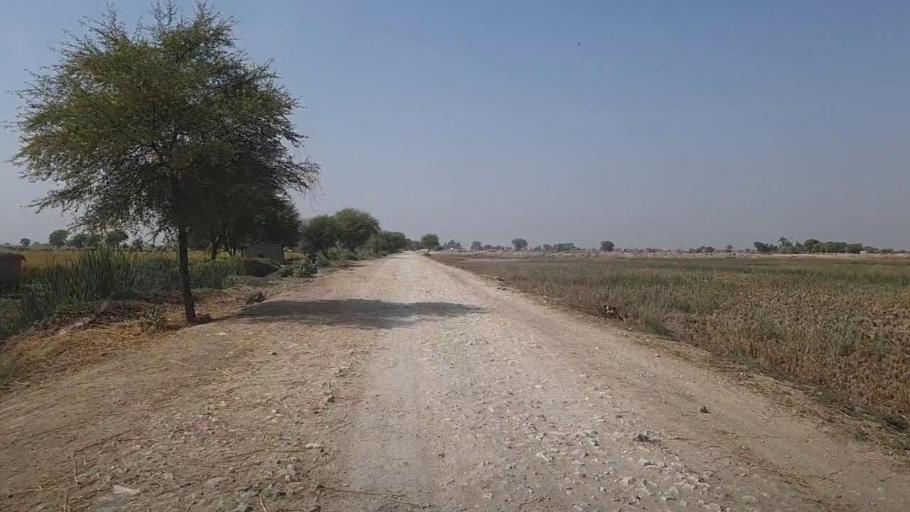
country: PK
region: Sindh
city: Kandhkot
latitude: 28.3927
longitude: 69.3025
